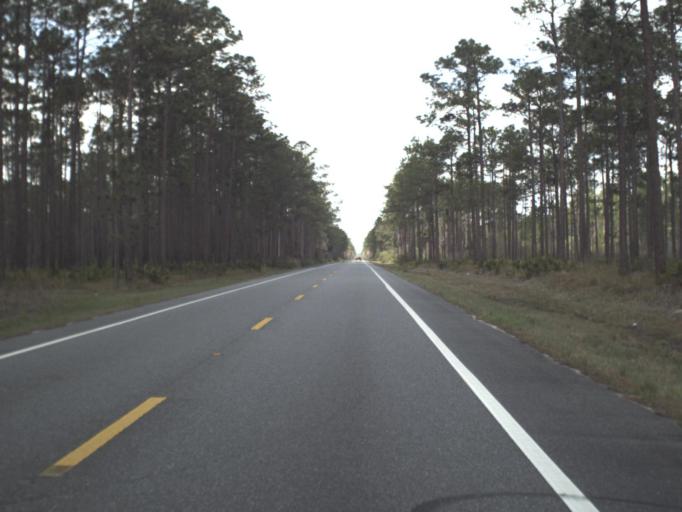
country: US
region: Florida
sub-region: Franklin County
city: Apalachicola
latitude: 29.9790
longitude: -84.9753
